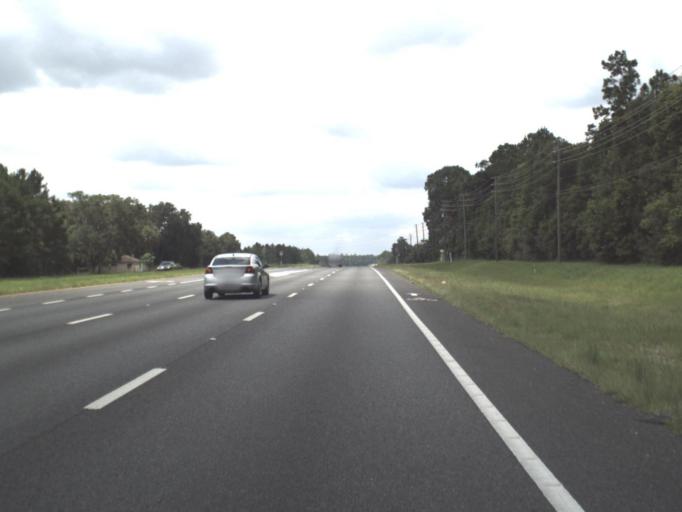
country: US
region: Florida
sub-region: Hernando County
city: South Brooksville
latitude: 28.5083
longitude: -82.4214
